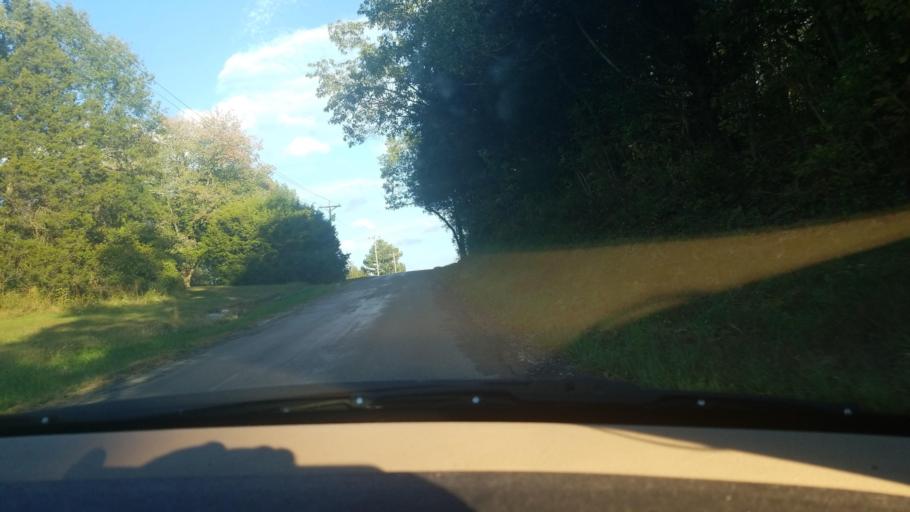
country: US
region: Illinois
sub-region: Saline County
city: Carrier Mills
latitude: 37.7712
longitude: -88.7593
